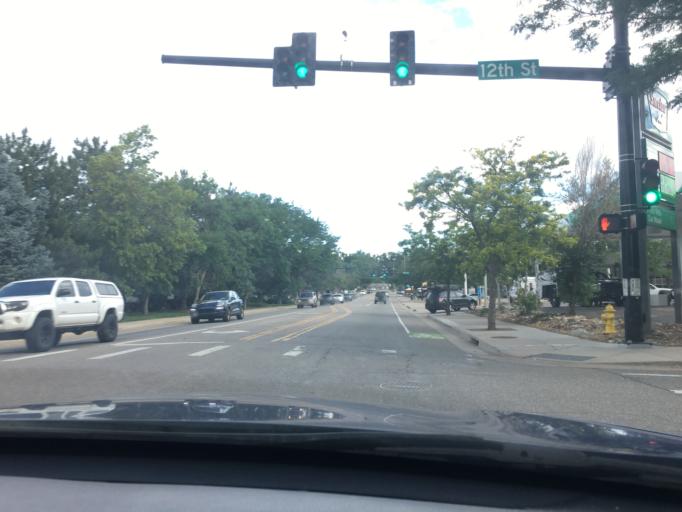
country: US
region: Colorado
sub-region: Jefferson County
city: Golden
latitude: 39.7566
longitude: -105.2193
